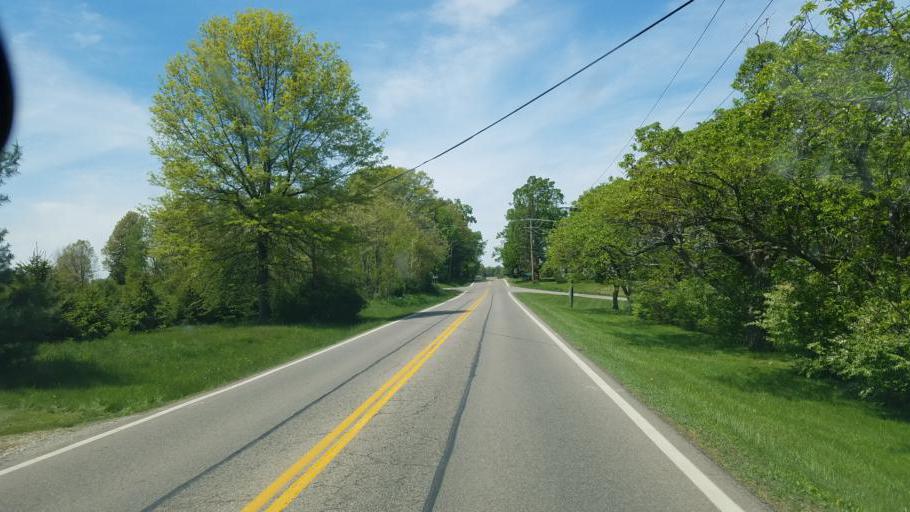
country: US
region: Ohio
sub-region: Knox County
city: Gambier
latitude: 40.3887
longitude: -82.4025
